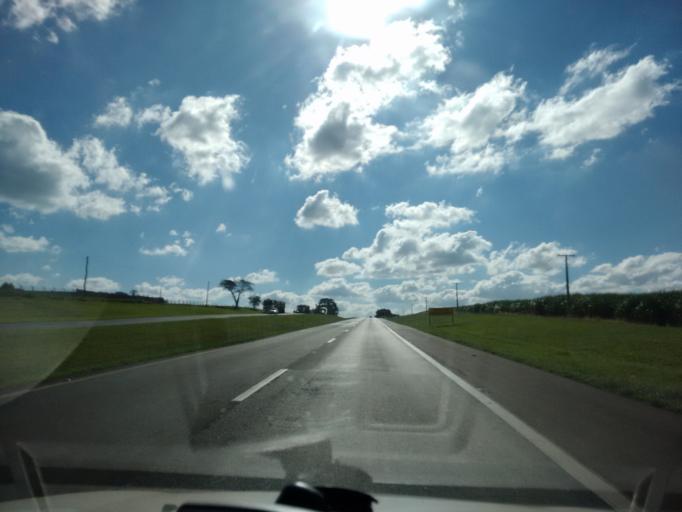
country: BR
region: Sao Paulo
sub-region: Ibate
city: Ibate
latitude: -21.9091
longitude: -48.0502
